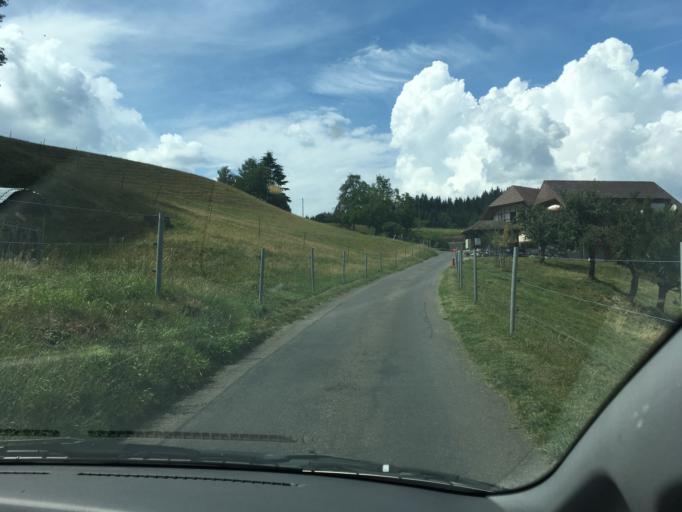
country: CH
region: Bern
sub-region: Bern-Mittelland District
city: Stettlen
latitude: 46.9429
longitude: 7.5344
